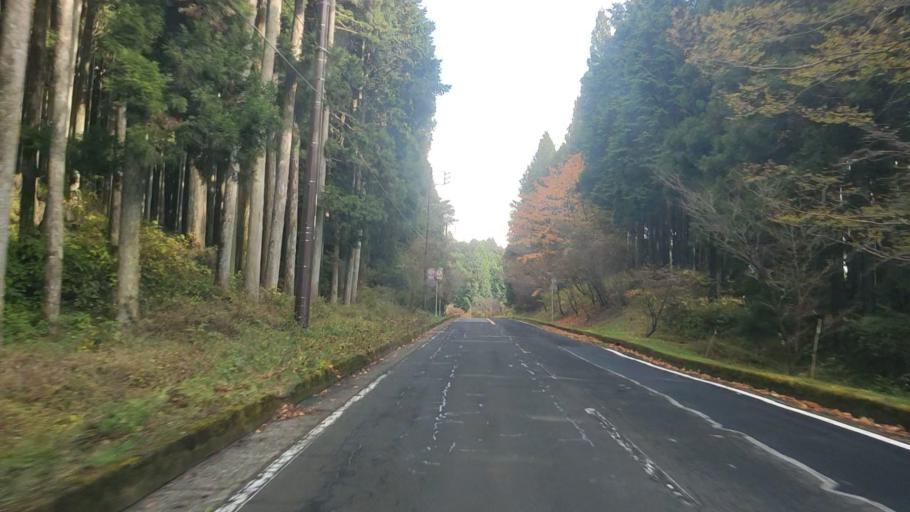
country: JP
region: Shizuoka
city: Fujinomiya
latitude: 35.3041
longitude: 138.6763
